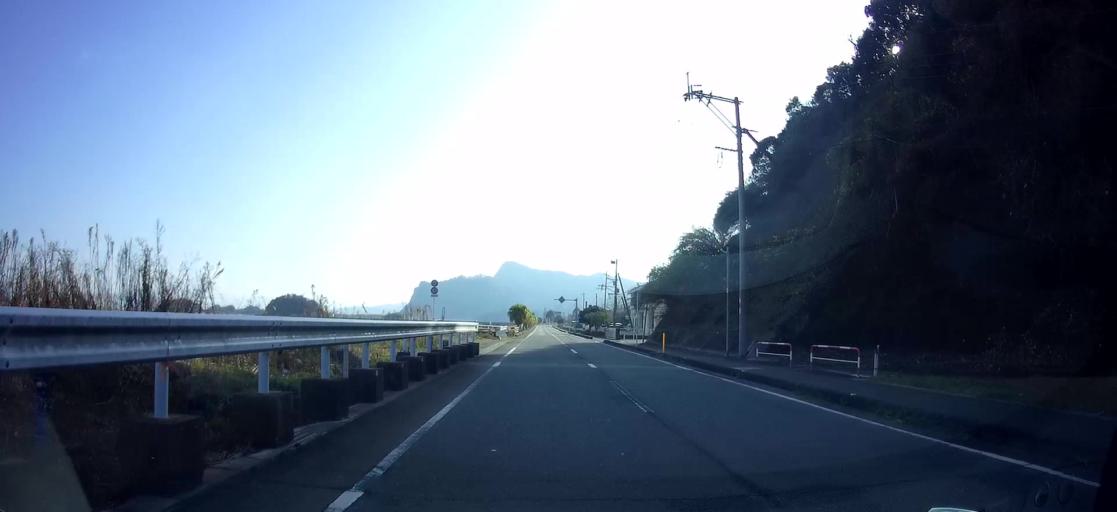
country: JP
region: Kumamoto
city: Yatsushiro
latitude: 32.4461
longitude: 130.4158
